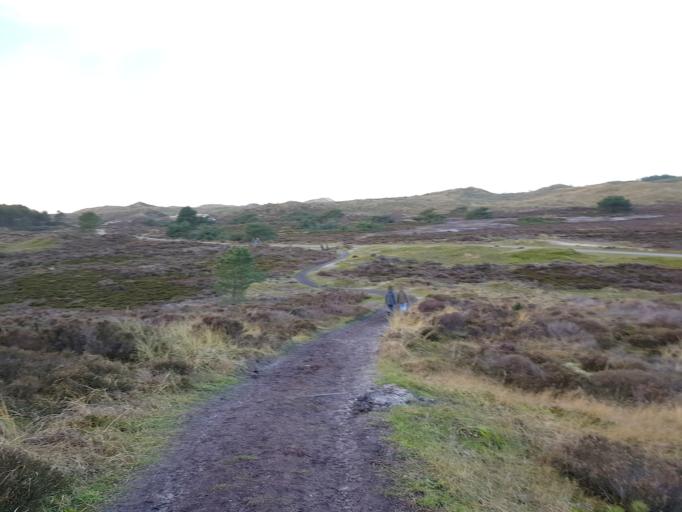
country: NL
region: North Holland
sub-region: Gemeente Bergen
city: Egmond aan Zee
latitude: 52.6998
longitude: 4.6533
